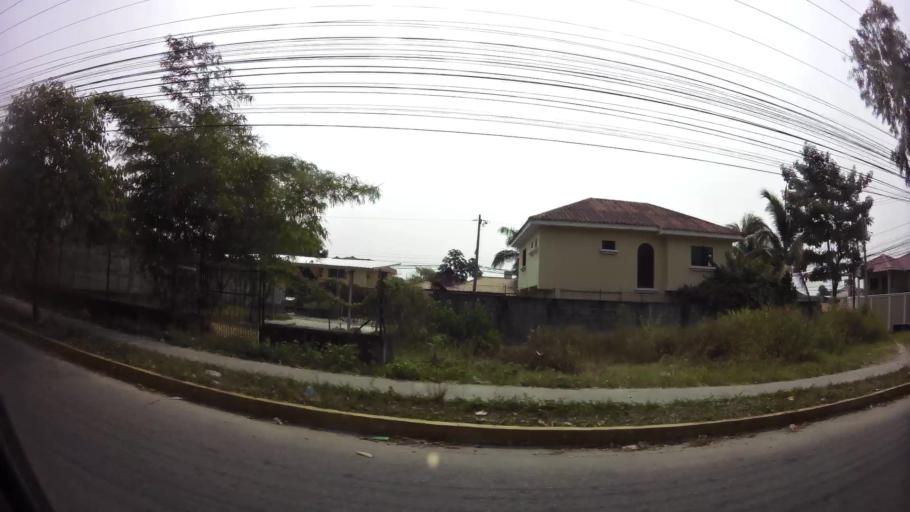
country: HN
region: Cortes
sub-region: San Pedro Sula
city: Pena Blanca
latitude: 15.5430
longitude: -88.0329
